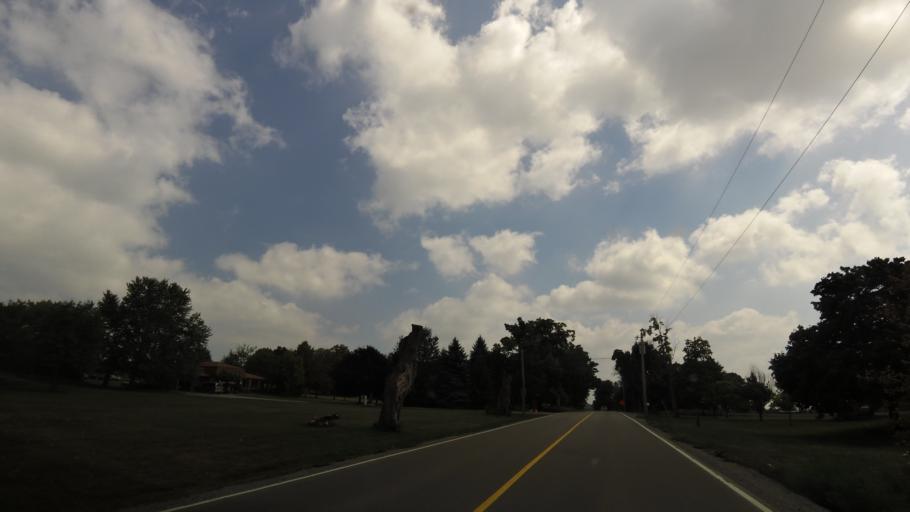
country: CA
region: Ontario
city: Oshawa
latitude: 43.9890
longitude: -78.8712
